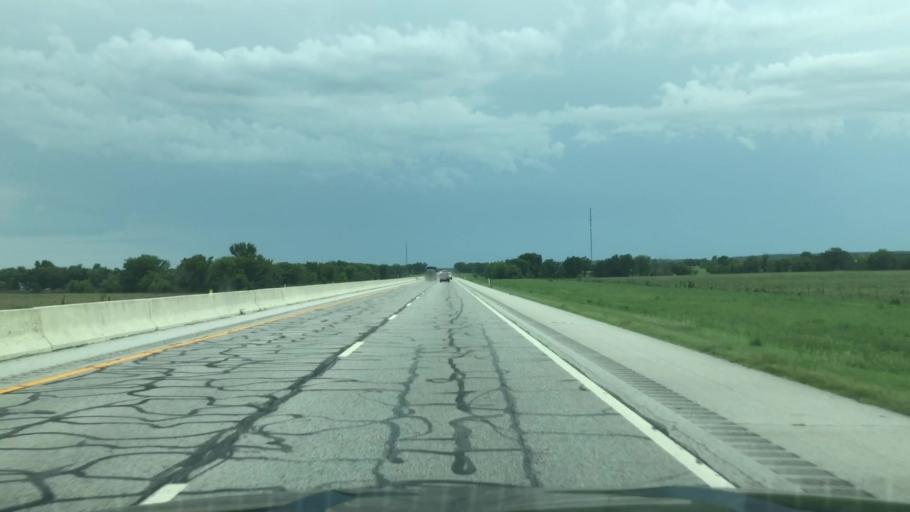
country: US
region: Oklahoma
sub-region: Craig County
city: Vinita
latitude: 36.5164
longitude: -95.2640
